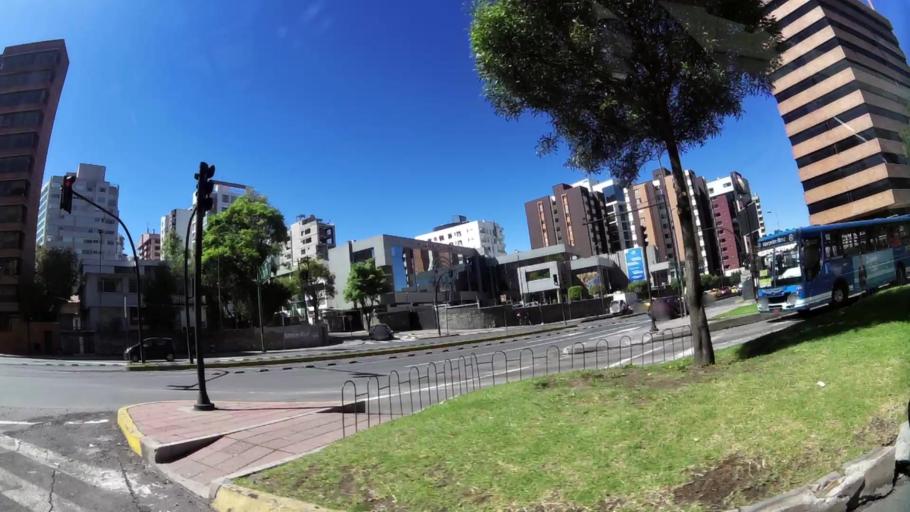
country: EC
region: Pichincha
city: Quito
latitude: -0.1871
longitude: -78.4798
